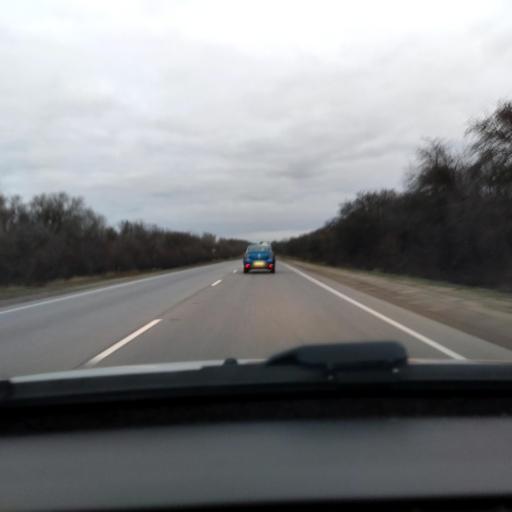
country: RU
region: Lipetsk
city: Borinskoye
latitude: 52.4339
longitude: 39.2708
